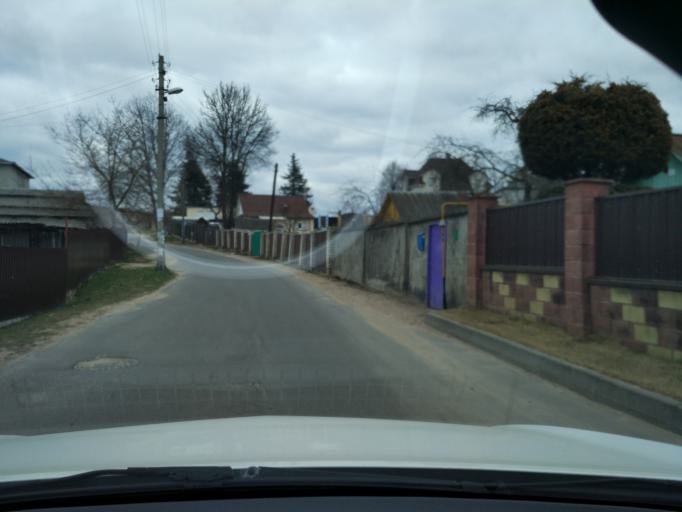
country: BY
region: Minsk
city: Bal'shavik
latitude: 53.9674
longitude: 27.5963
